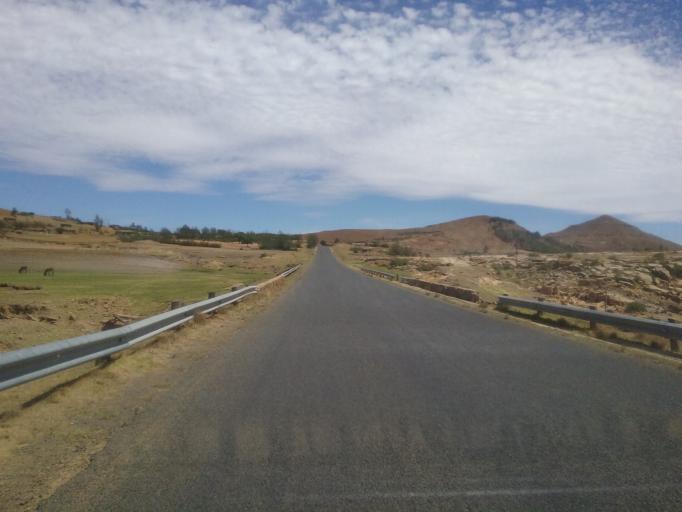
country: LS
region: Mafeteng
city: Mafeteng
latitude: -29.9229
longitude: 27.2544
